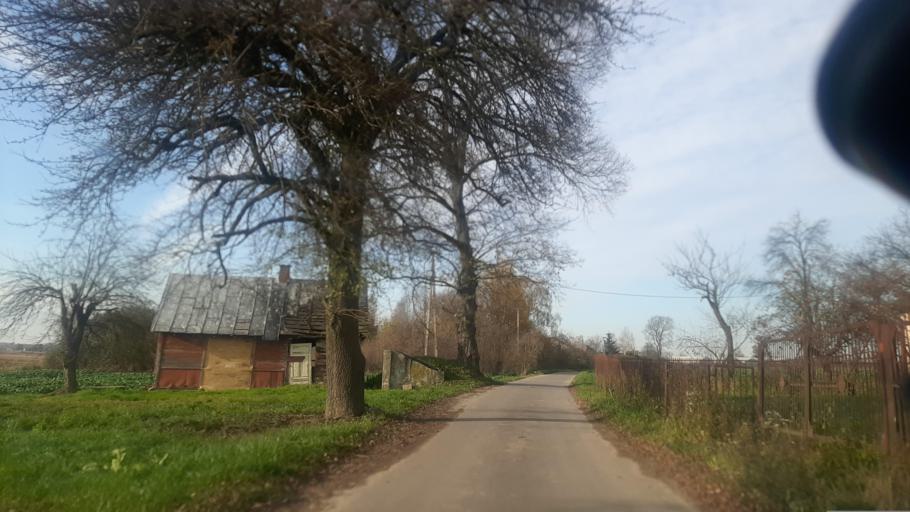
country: PL
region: Lublin Voivodeship
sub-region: Powiat pulawski
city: Markuszow
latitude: 51.3661
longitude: 22.2737
